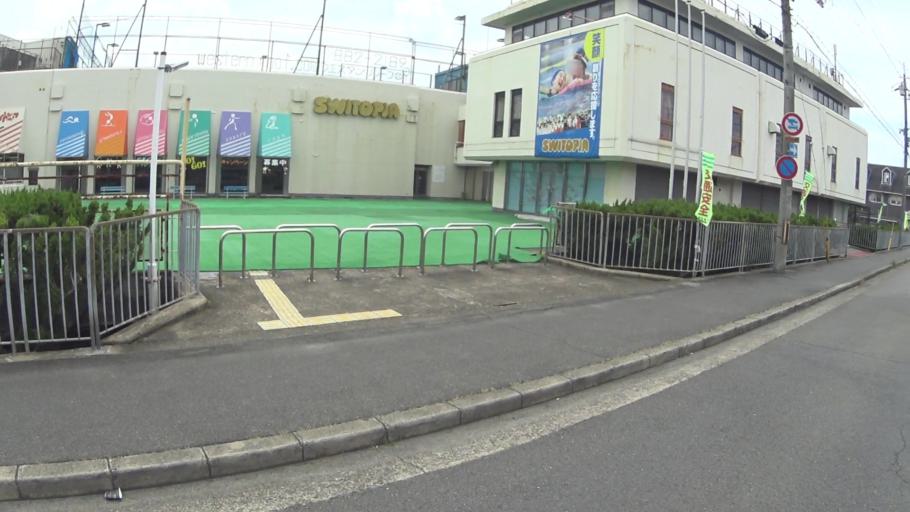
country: JP
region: Kyoto
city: Kyoto
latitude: 35.0163
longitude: 135.7151
